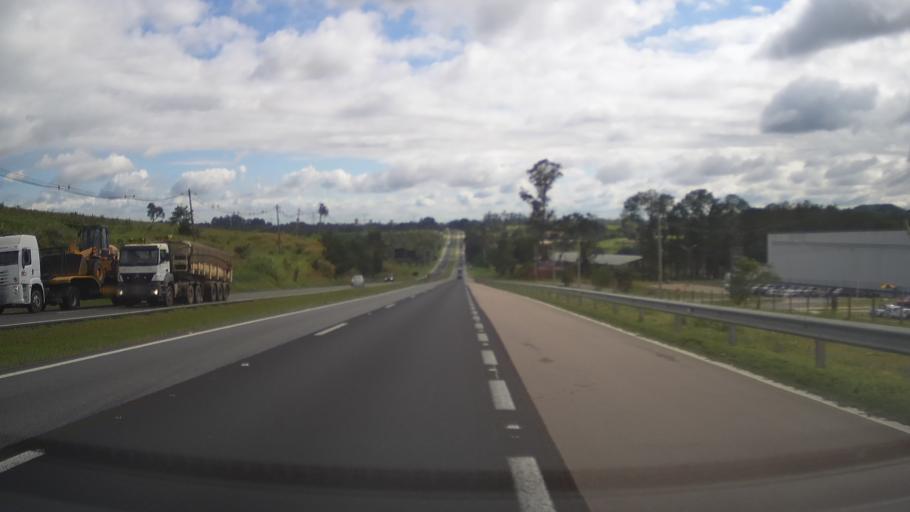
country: BR
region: Sao Paulo
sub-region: Itupeva
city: Itupeva
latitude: -23.2249
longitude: -47.0291
